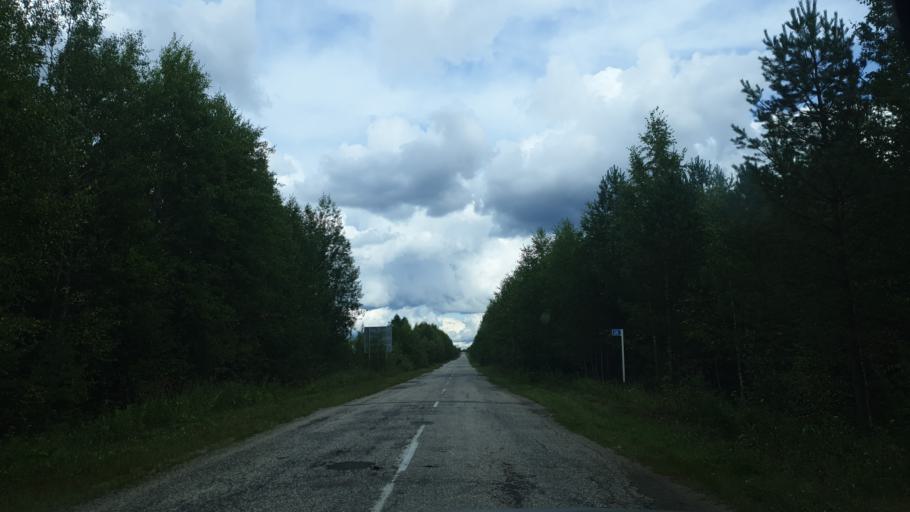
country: RU
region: Komi Republic
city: Aykino
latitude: 61.9366
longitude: 50.1570
